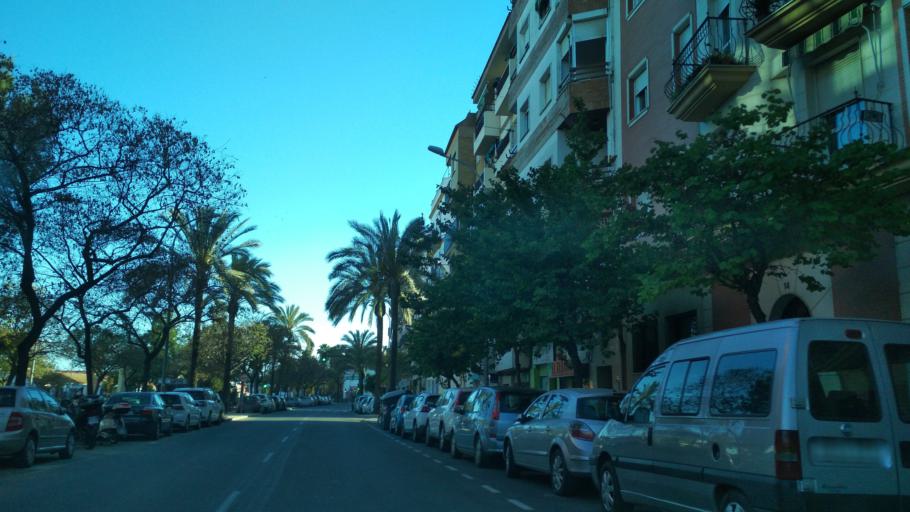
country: ES
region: Andalusia
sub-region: Provincia de Huelva
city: Huelva
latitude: 37.2669
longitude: -6.9520
